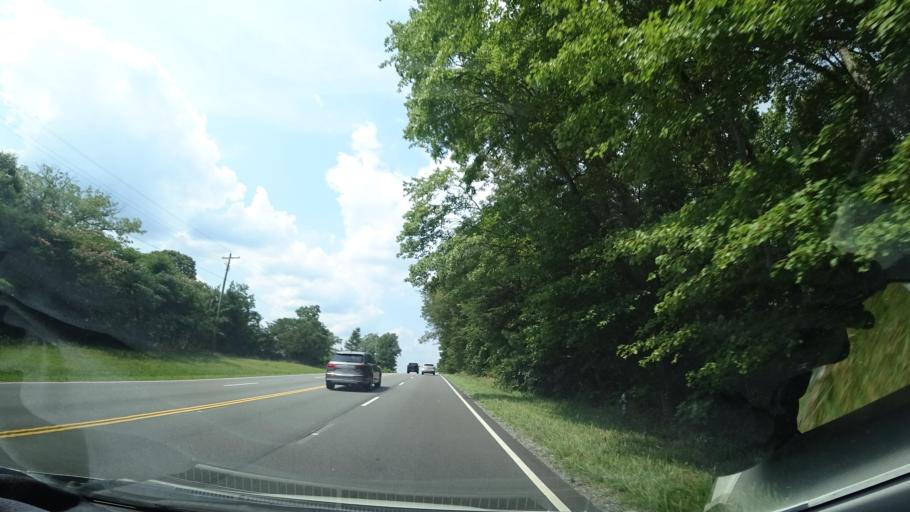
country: US
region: Virginia
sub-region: Hanover County
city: Ashland
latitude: 37.8525
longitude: -77.4636
